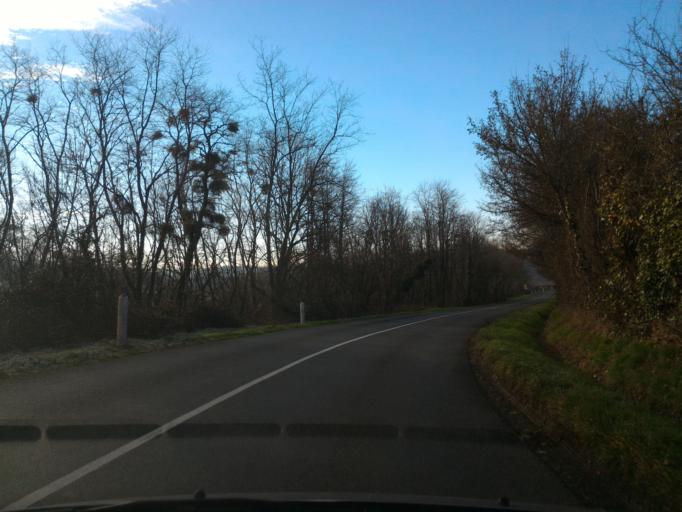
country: FR
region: Poitou-Charentes
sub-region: Departement de la Charente
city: Champagne-Mouton
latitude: 46.0255
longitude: 0.5241
